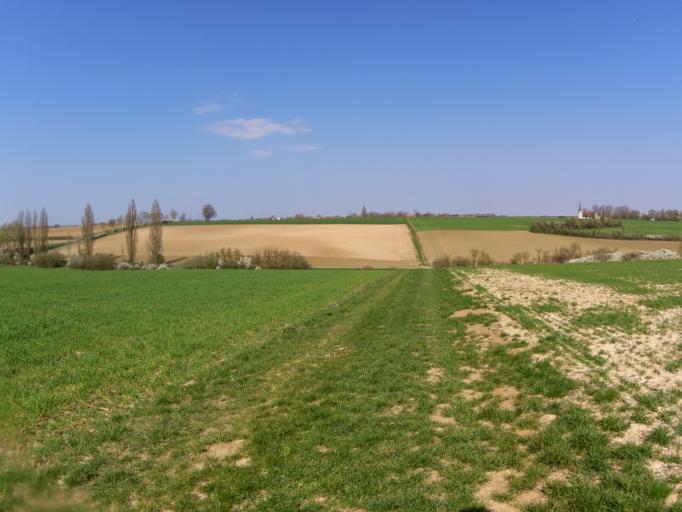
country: DE
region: Bavaria
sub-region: Regierungsbezirk Unterfranken
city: Mainstockheim
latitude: 49.8156
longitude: 10.1094
